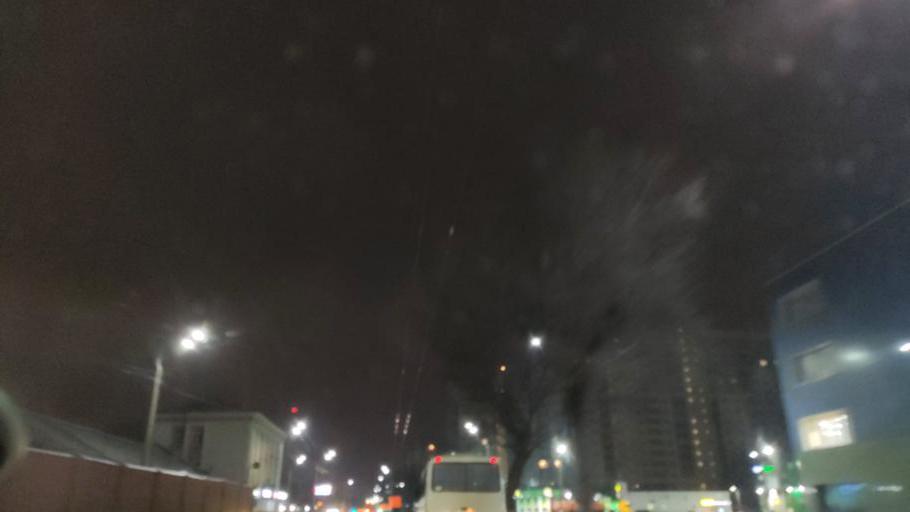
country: RU
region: Moskovskaya
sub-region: Podol'skiy Rayon
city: Podol'sk
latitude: 55.4277
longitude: 37.5558
